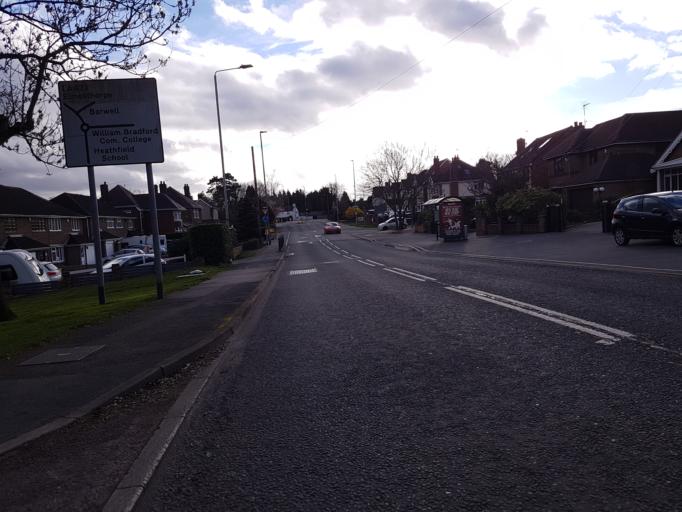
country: GB
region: England
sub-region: Leicestershire
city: Earl Shilton
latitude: 52.5709
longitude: -1.3296
